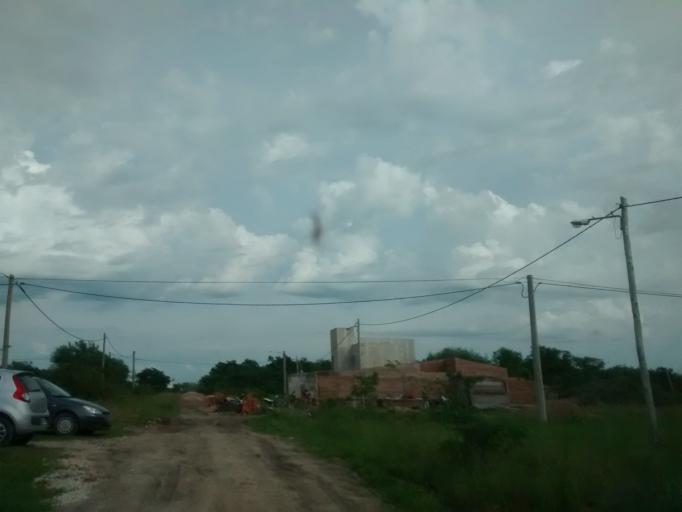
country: AR
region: Chaco
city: Resistencia
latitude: -27.4063
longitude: -58.9677
